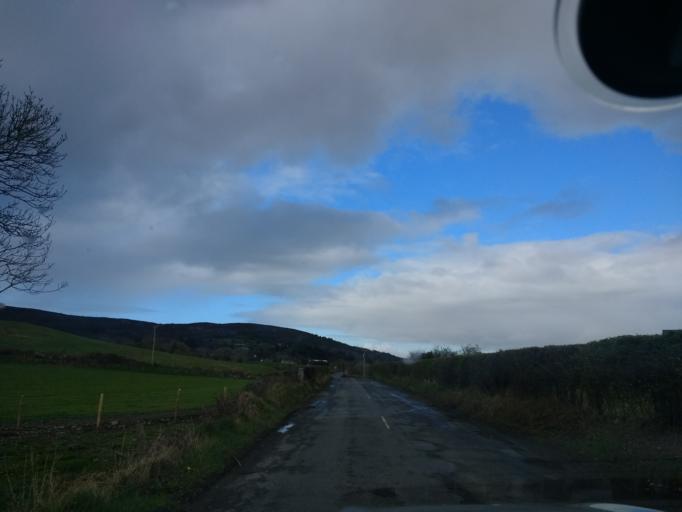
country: IE
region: Ulster
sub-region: County Donegal
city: Buncrana
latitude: 55.1038
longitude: -7.5345
